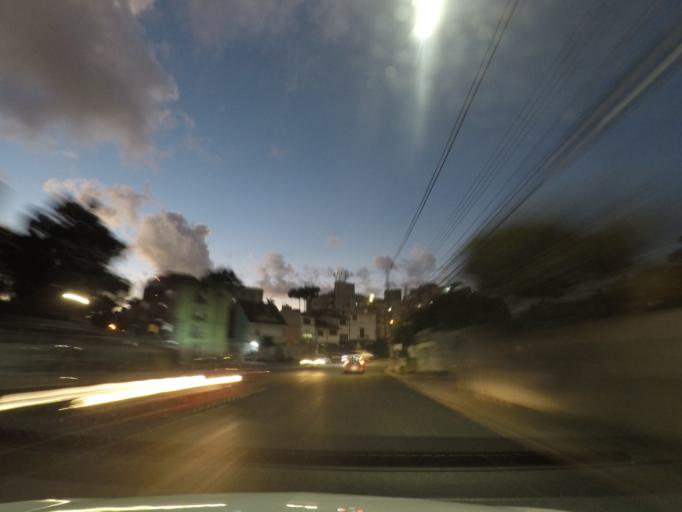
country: BR
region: Parana
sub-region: Curitiba
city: Curitiba
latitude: -25.4617
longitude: -49.2784
